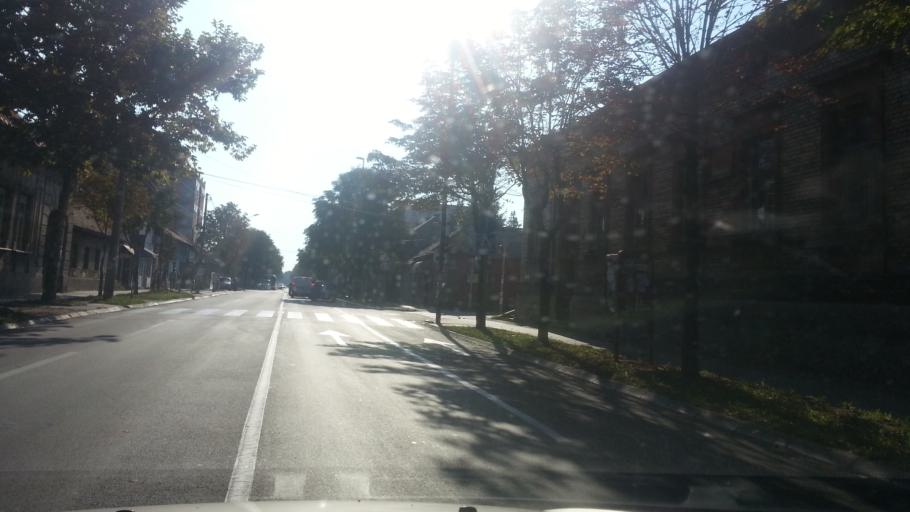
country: RS
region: Central Serbia
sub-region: Belgrade
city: Zemun
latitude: 44.8513
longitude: 20.3971
